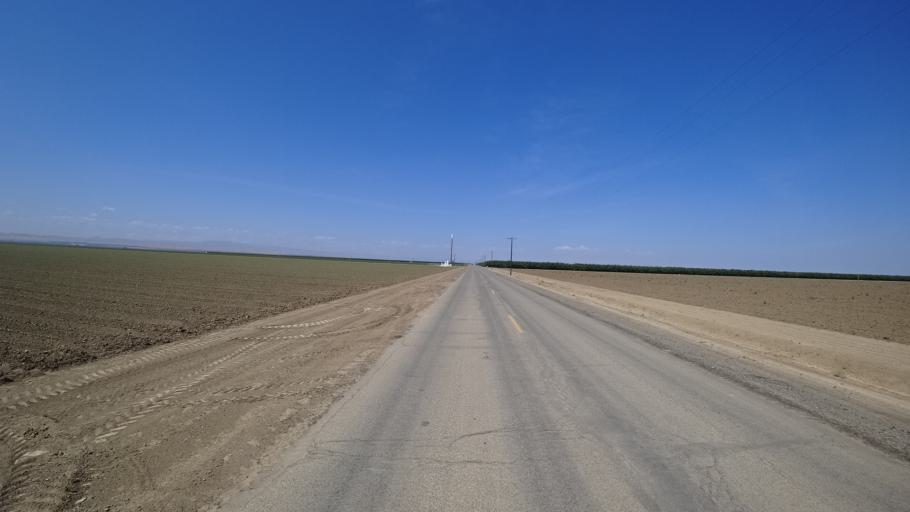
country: US
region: California
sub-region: Fresno County
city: Huron
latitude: 36.1377
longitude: -119.9916
